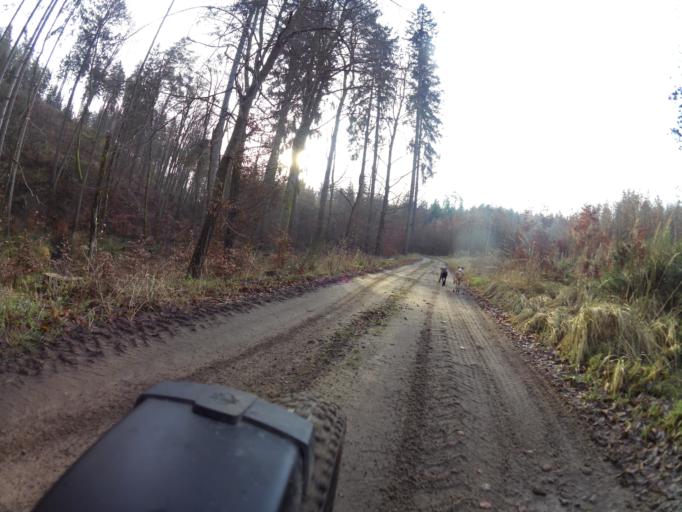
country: PL
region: West Pomeranian Voivodeship
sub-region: Powiat koszalinski
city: Polanow
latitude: 54.1848
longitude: 16.7200
